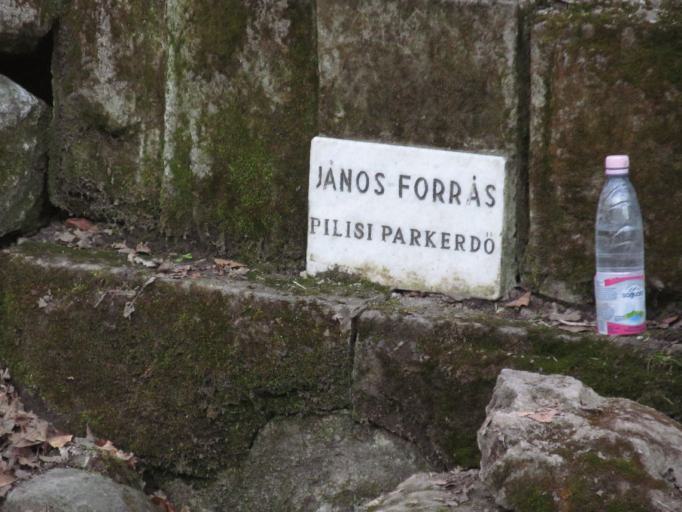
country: HU
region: Pest
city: Nagykovacsi
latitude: 47.6728
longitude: 19.0094
